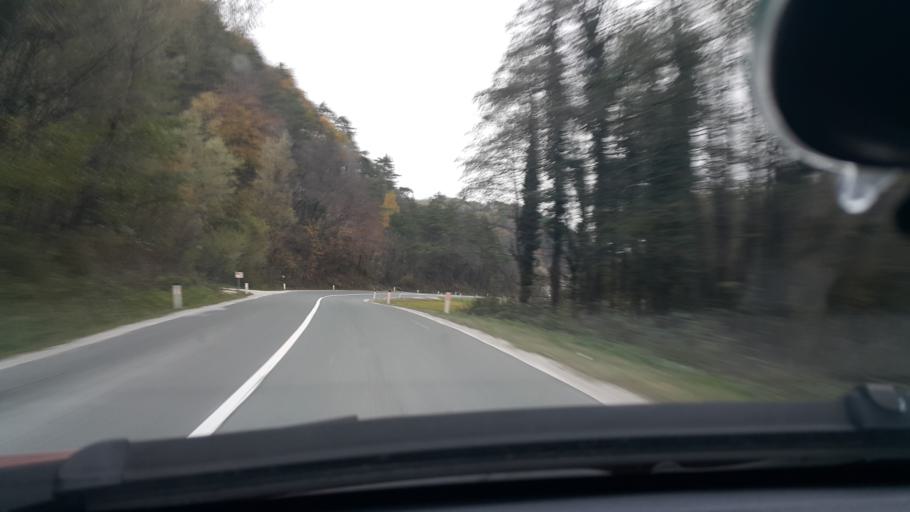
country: SI
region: Poljcane
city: Poljcane
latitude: 46.2898
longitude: 15.5705
